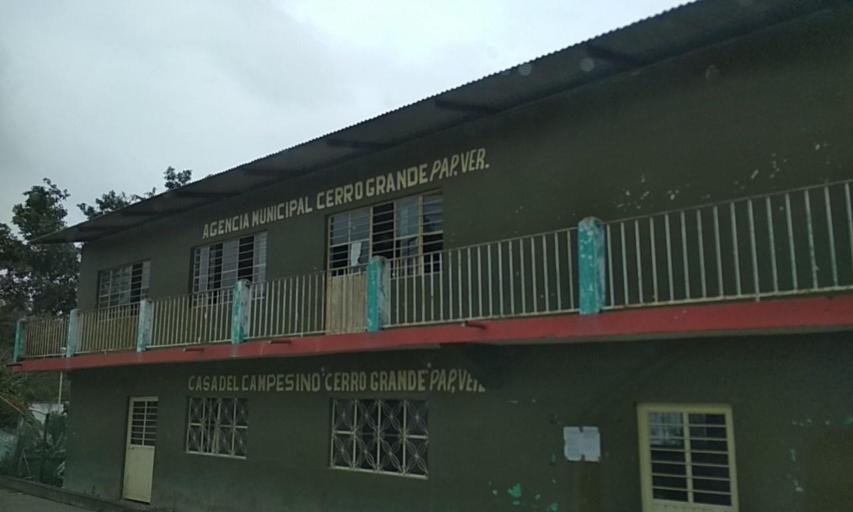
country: MX
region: Veracruz
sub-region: Papantla
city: El Chote
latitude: 20.3833
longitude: -97.3519
